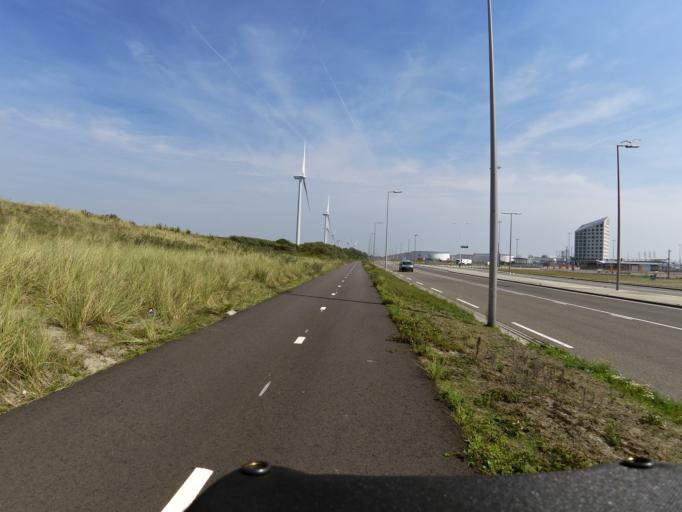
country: NL
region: South Holland
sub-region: Gemeente Rotterdam
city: Hoek van Holland
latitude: 51.9830
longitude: 4.0395
